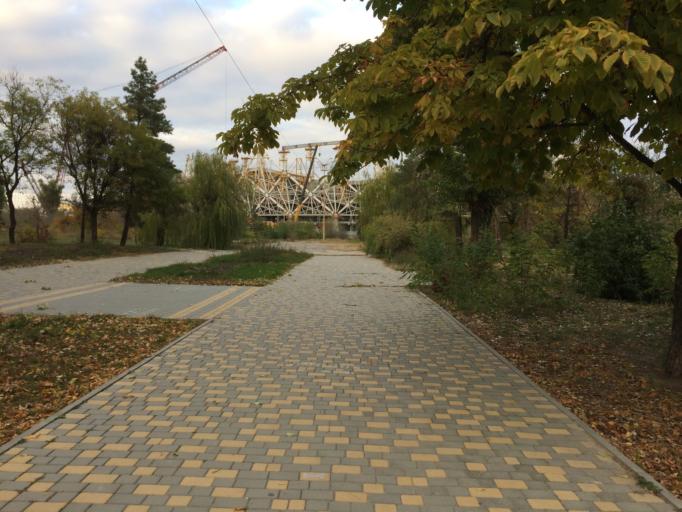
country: RU
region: Volgograd
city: Krasnoslobodsk
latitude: 48.7317
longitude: 44.5461
